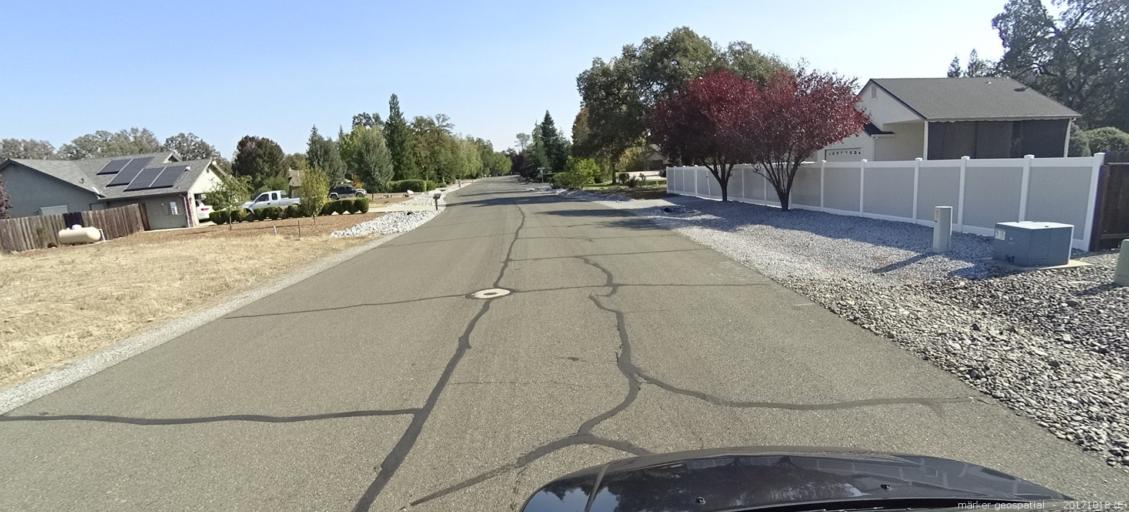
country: US
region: California
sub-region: Shasta County
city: Palo Cedro
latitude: 40.5597
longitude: -122.2365
